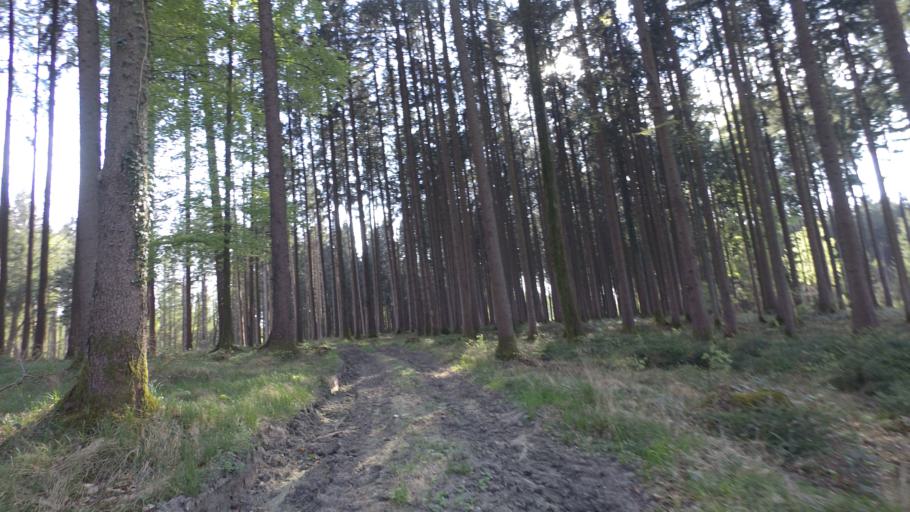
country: DE
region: Bavaria
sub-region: Upper Bavaria
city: Chieming
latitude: 47.9184
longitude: 12.5090
